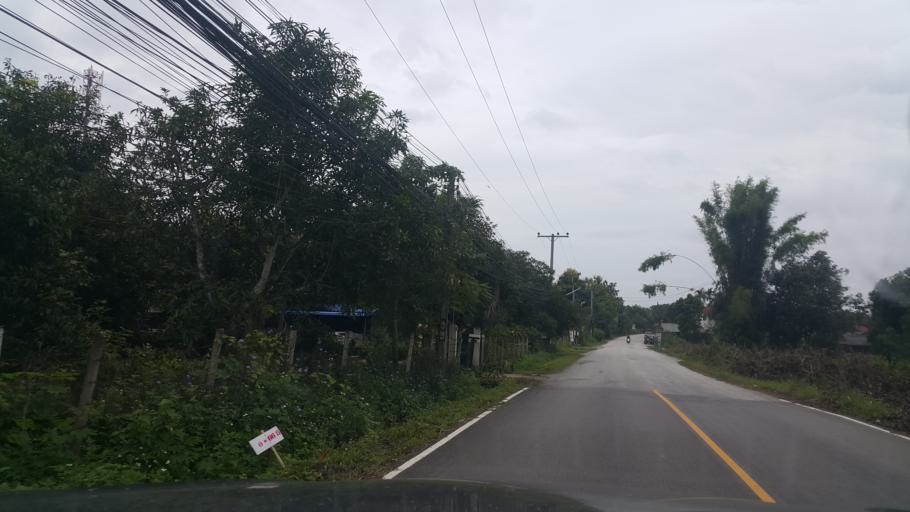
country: TH
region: Chiang Mai
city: San Sai
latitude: 18.9111
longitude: 99.0173
